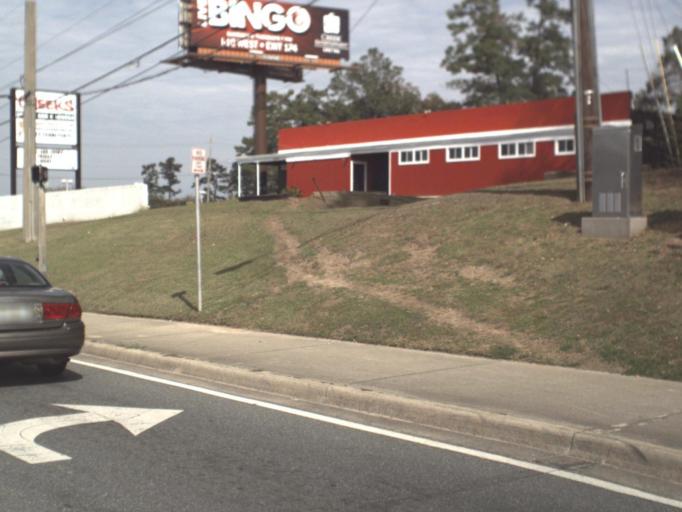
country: US
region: Florida
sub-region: Leon County
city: Tallahassee
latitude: 30.4470
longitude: -84.3257
